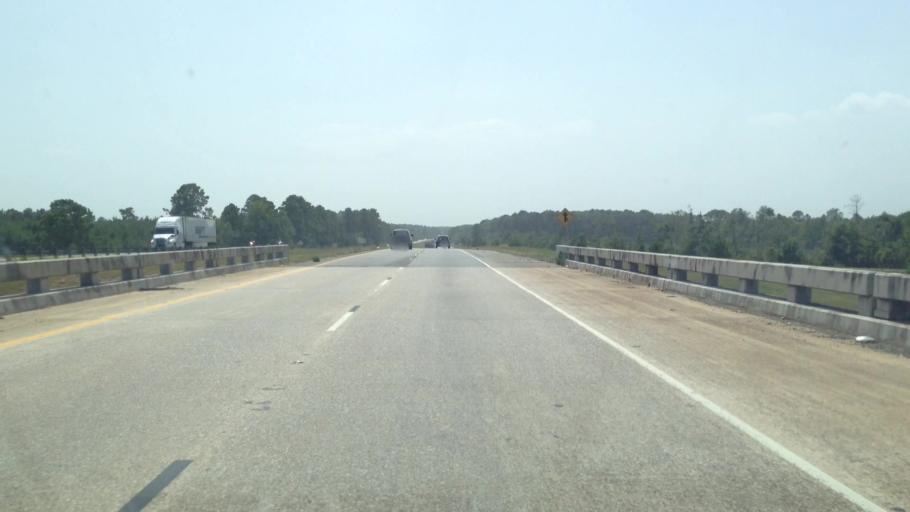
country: US
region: Louisiana
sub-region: Bossier Parish
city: Haughton
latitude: 32.5790
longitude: -93.4320
